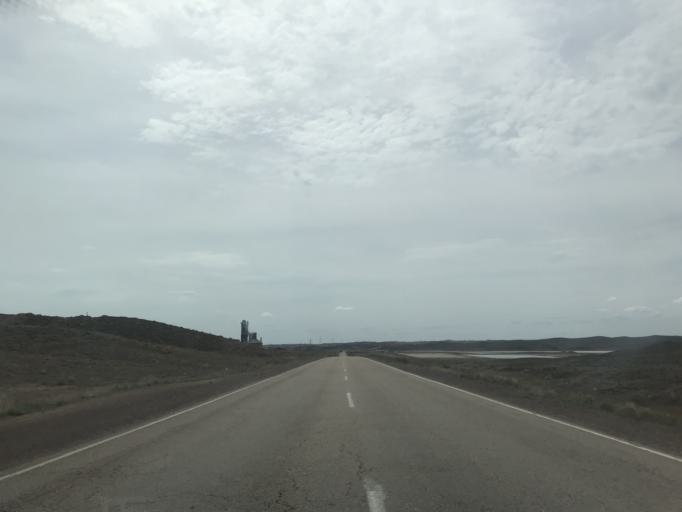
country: KZ
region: Zhambyl
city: Mynaral
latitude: 45.4019
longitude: 73.6372
